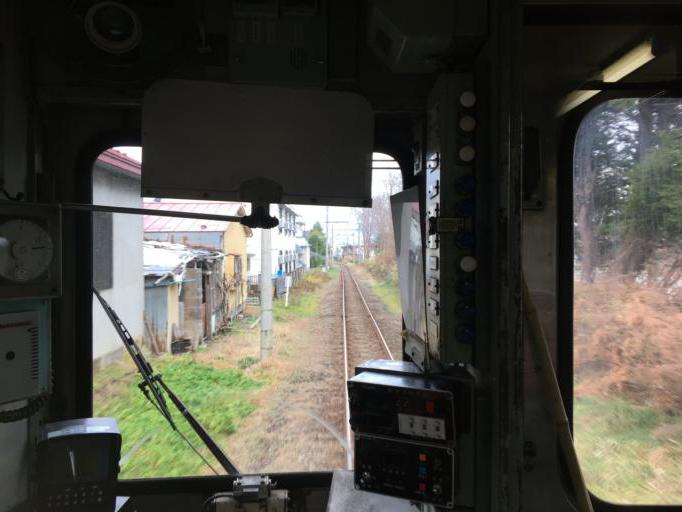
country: JP
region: Aomori
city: Hirosaki
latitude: 40.5787
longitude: 140.4722
